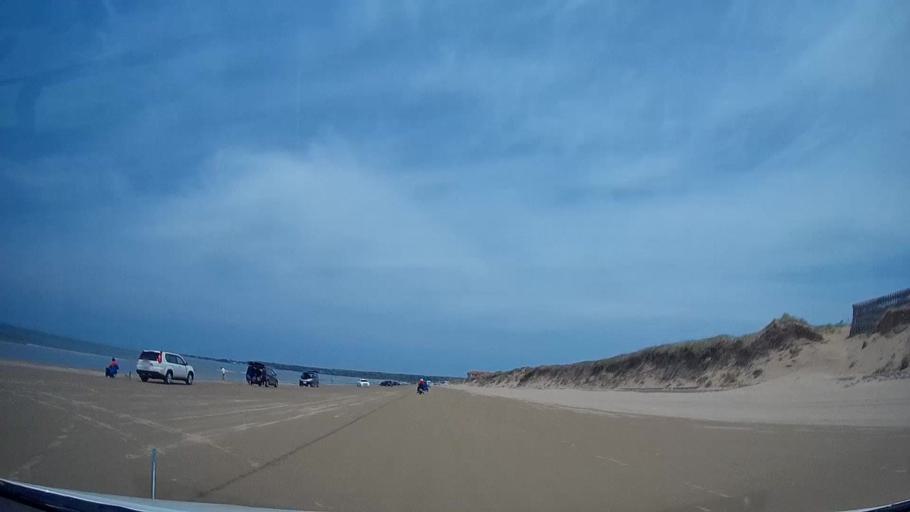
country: JP
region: Ishikawa
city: Hakui
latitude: 36.8885
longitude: 136.7645
